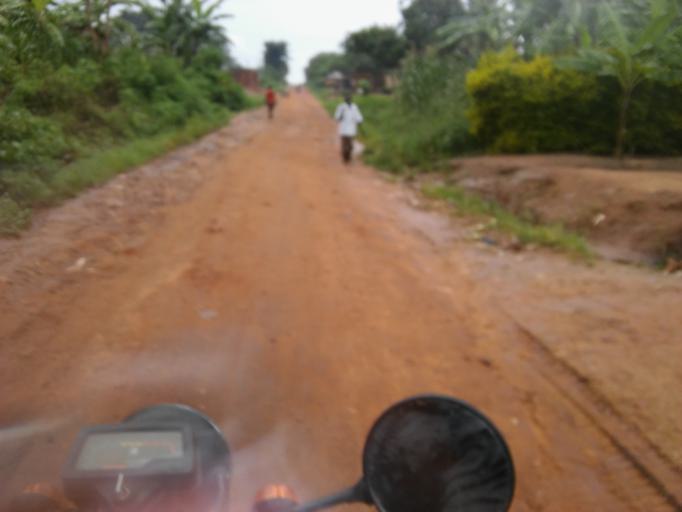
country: UG
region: Eastern Region
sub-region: Mbale District
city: Mbale
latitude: 1.0167
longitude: 34.1849
